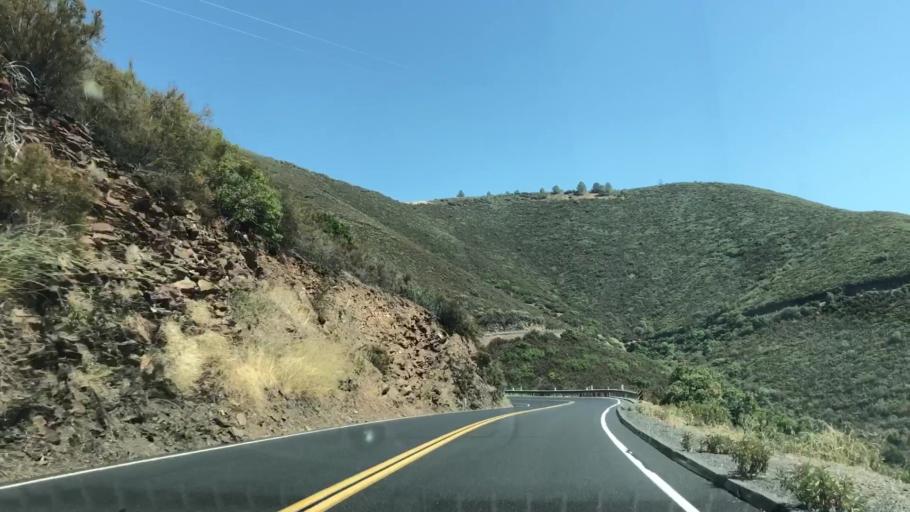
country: US
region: California
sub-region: Tuolumne County
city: Tuolumne City
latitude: 37.8232
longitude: -120.2810
